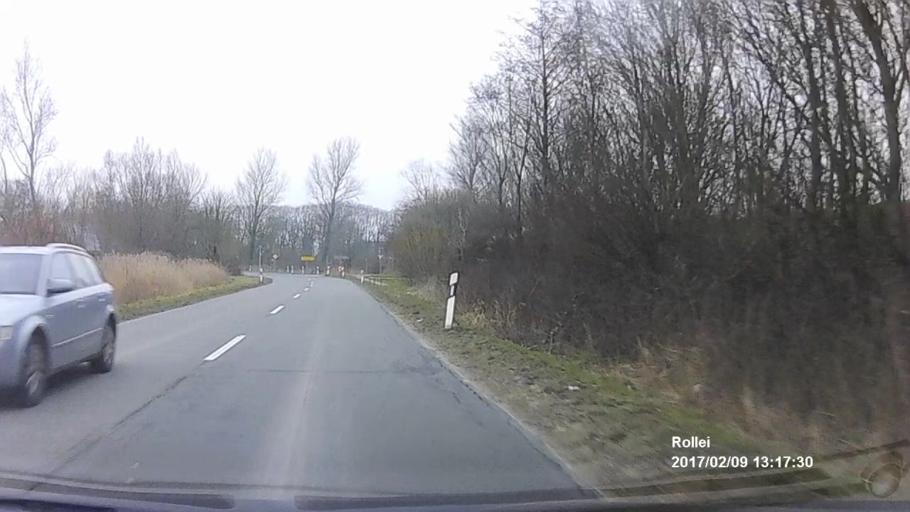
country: DE
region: Lower Saxony
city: Hinte
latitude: 53.4205
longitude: 7.1846
